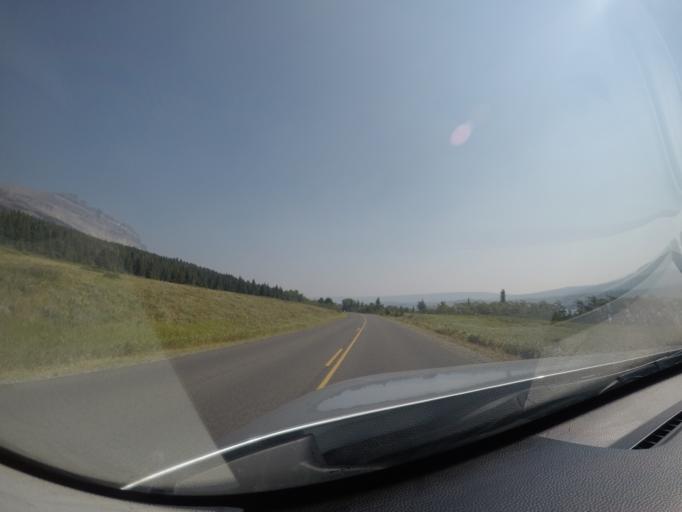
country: US
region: Montana
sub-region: Glacier County
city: Browning
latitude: 48.6963
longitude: -113.5117
